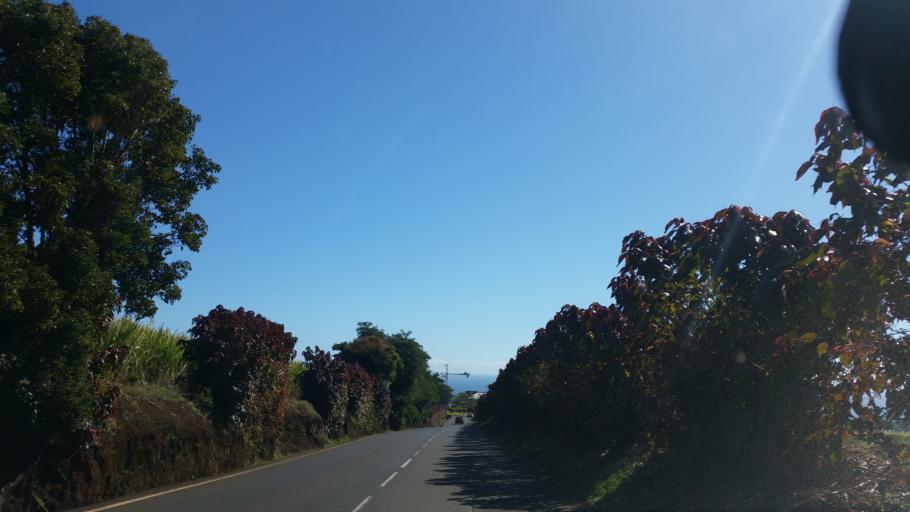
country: RE
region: Reunion
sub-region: Reunion
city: Sainte-Marie
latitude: -20.9270
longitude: 55.5304
